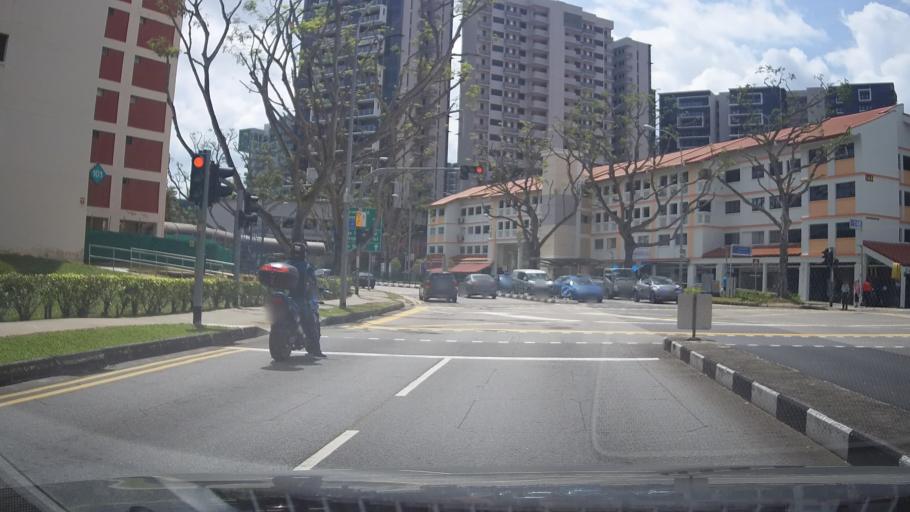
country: SG
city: Singapore
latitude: 1.3334
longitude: 103.8681
